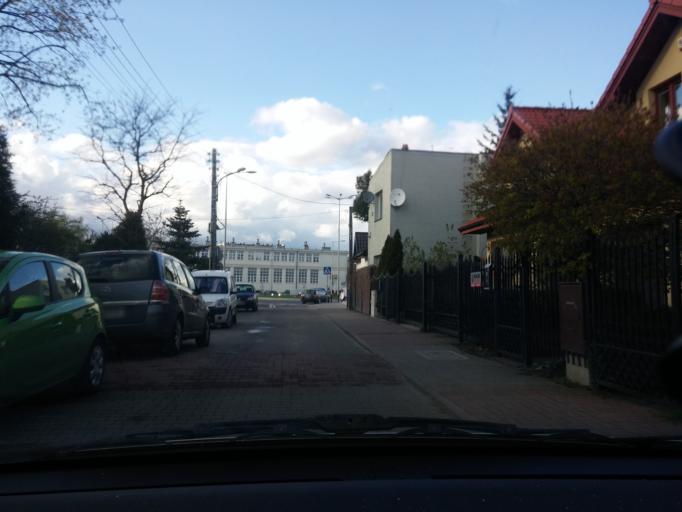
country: PL
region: Masovian Voivodeship
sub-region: Warszawa
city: Wawer
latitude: 52.2047
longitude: 21.1712
